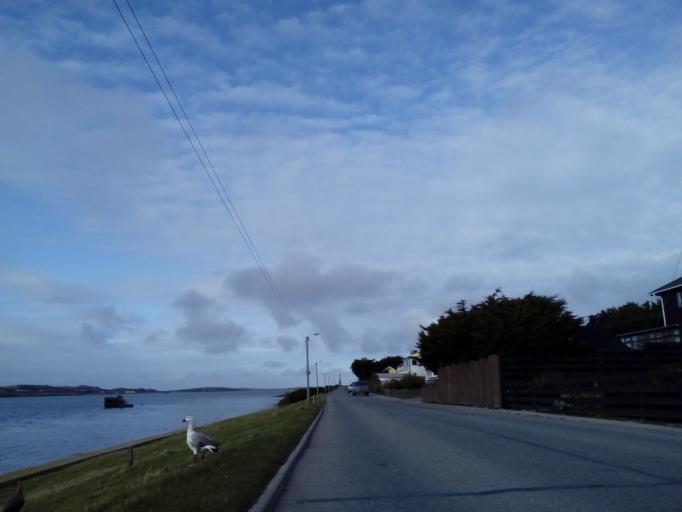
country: FK
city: Stanley
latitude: -51.6903
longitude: -57.8821
